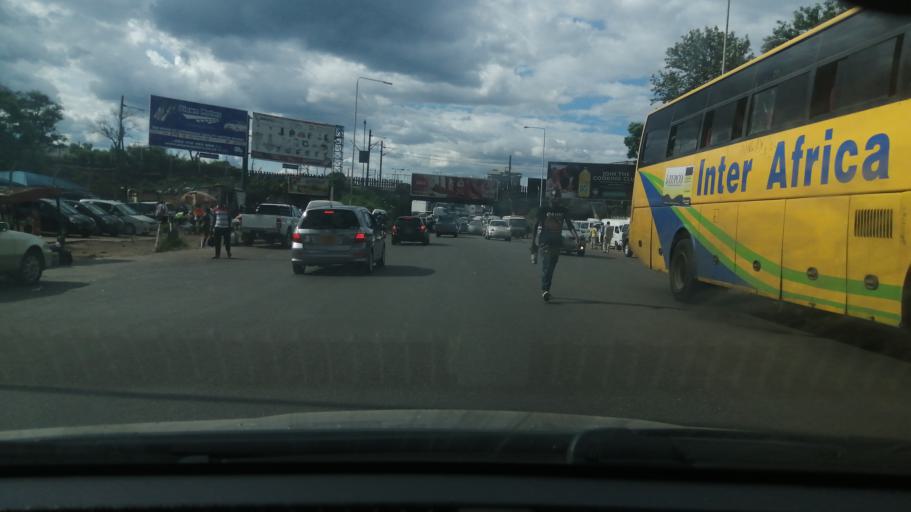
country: ZW
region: Harare
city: Harare
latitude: -17.8378
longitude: 31.0475
